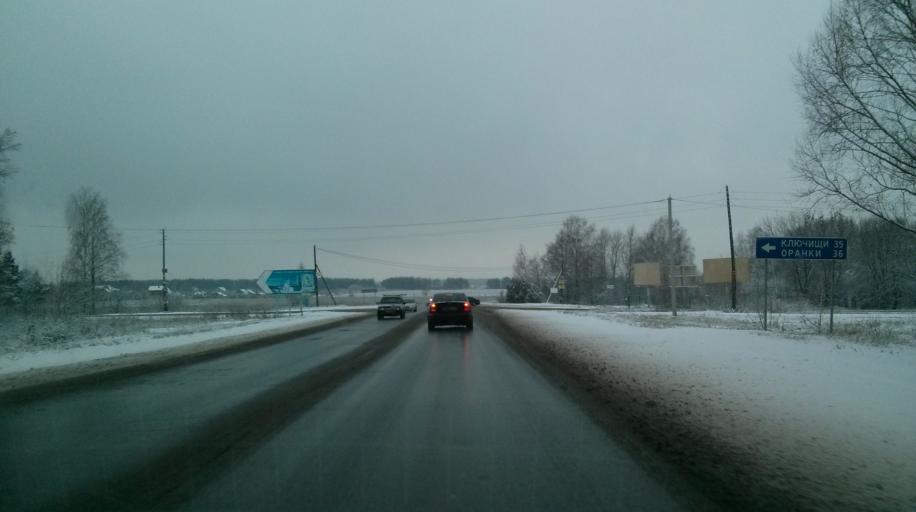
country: RU
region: Nizjnij Novgorod
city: Bogorodsk
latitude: 56.0871
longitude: 43.5305
